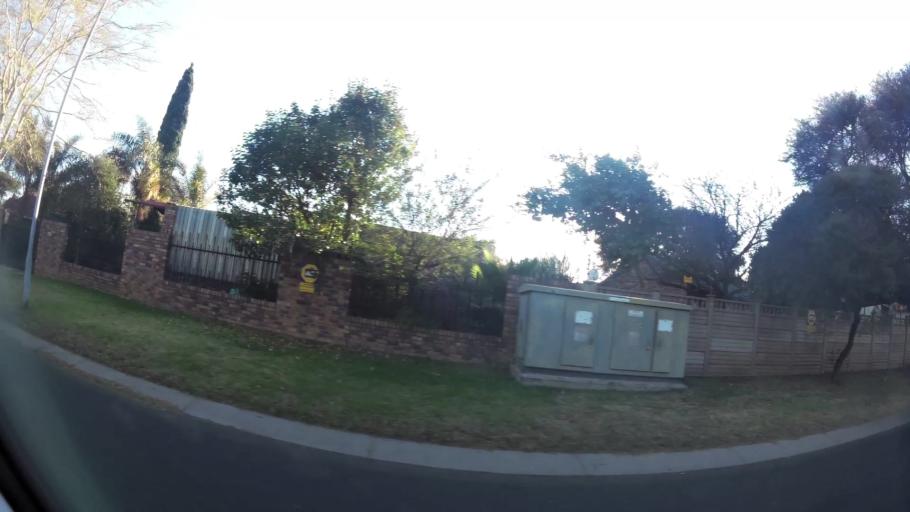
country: ZA
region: Gauteng
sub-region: City of Tshwane Metropolitan Municipality
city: Centurion
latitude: -25.9005
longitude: 28.1324
